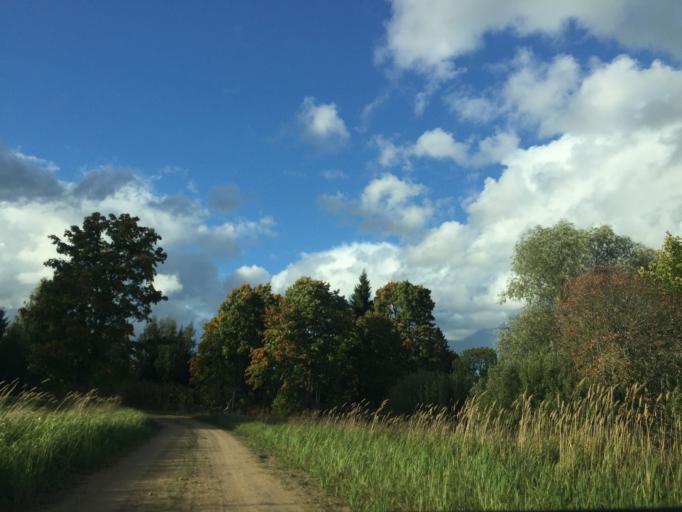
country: LV
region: Ligatne
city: Ligatne
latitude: 57.1306
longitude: 25.1251
